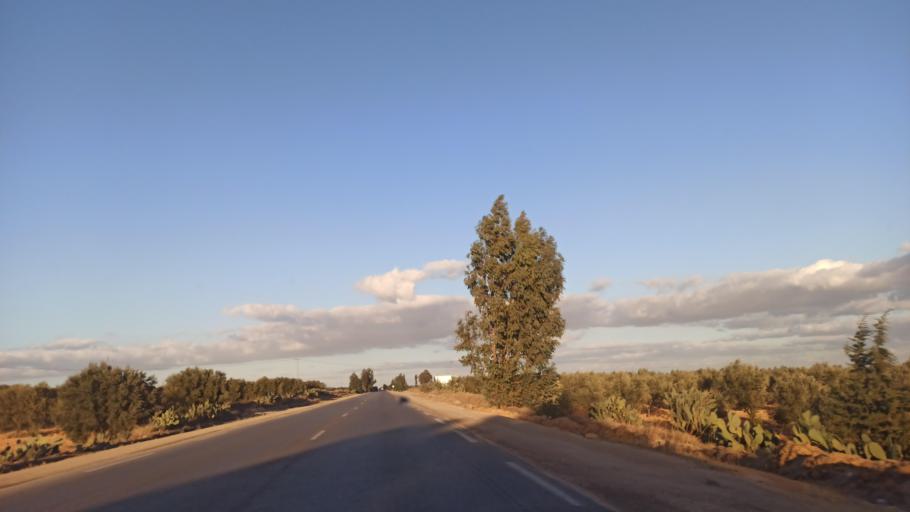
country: TN
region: Al Qayrawan
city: Sbikha
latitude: 35.8698
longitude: 10.2157
